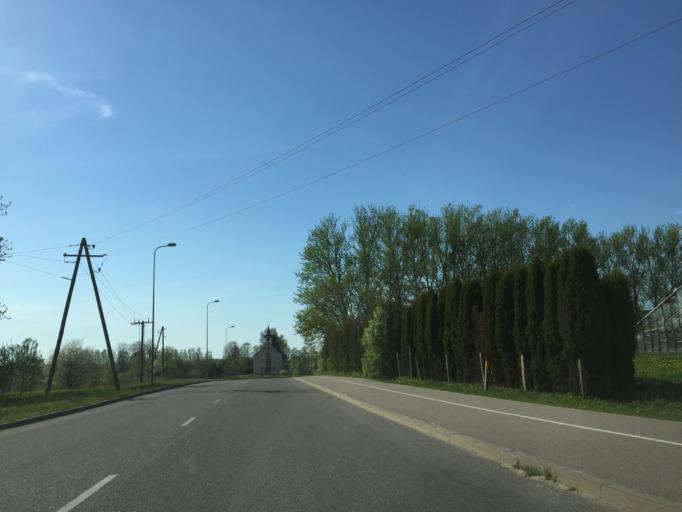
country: LV
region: Limbazu Rajons
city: Limbazi
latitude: 57.5166
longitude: 24.7232
